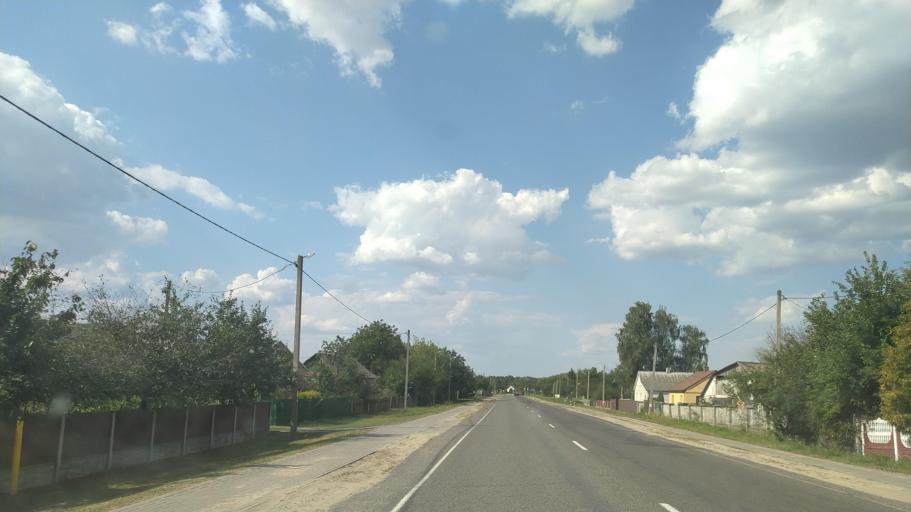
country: BY
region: Brest
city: Drahichyn
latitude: 52.2008
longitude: 25.1473
